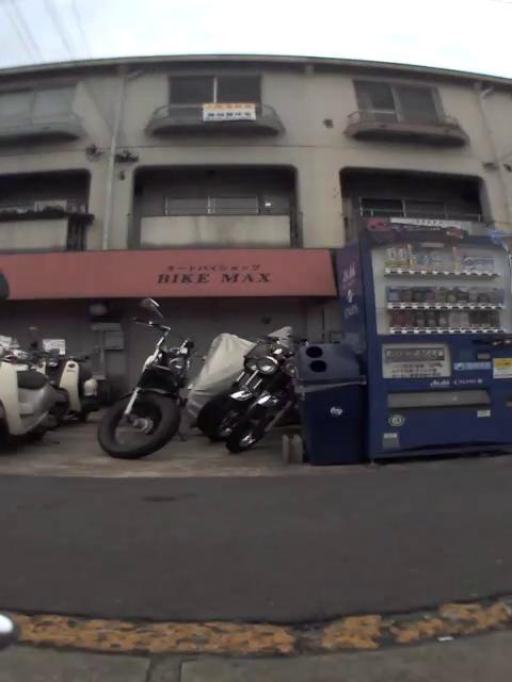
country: JP
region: Osaka
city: Neyagawa
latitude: 34.7730
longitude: 135.6316
